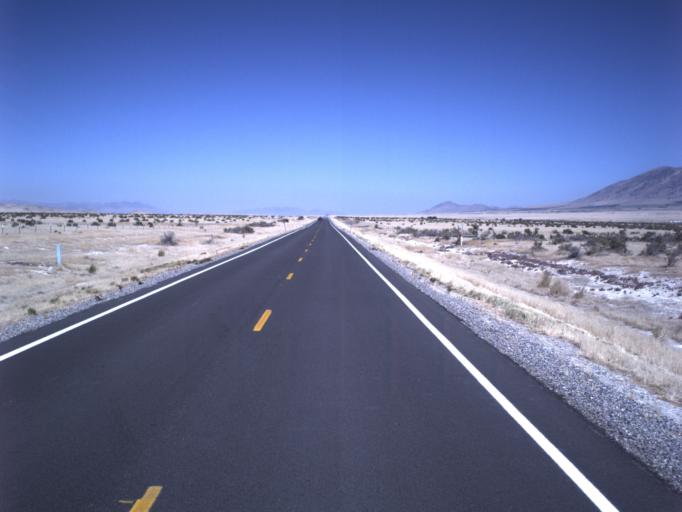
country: US
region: Utah
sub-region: Tooele County
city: Grantsville
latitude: 40.3090
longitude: -112.7432
